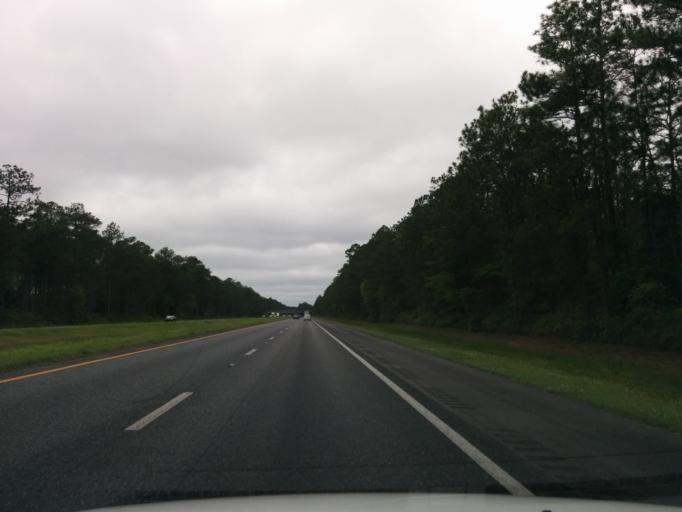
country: US
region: Florida
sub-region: Columbia County
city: Watertown
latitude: 30.2553
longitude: -82.4394
